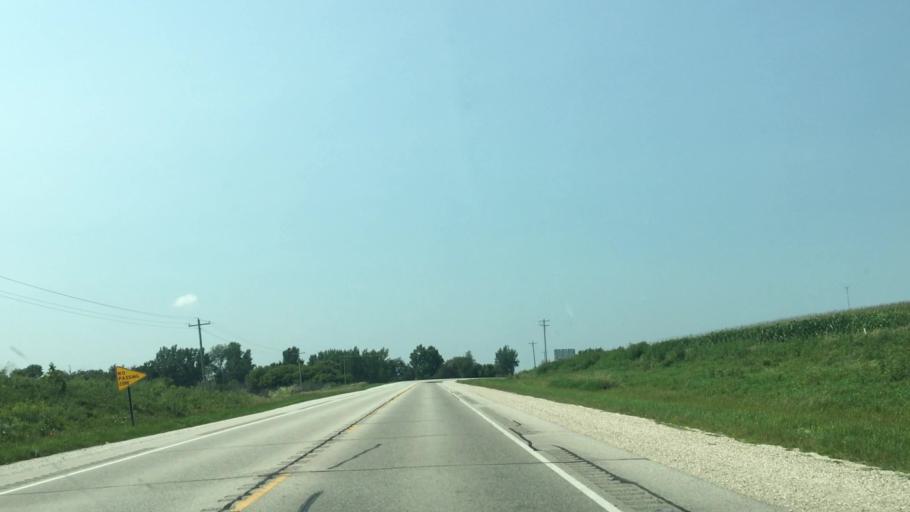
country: US
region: Iowa
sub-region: Winneshiek County
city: Decorah
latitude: 43.1928
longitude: -91.8700
